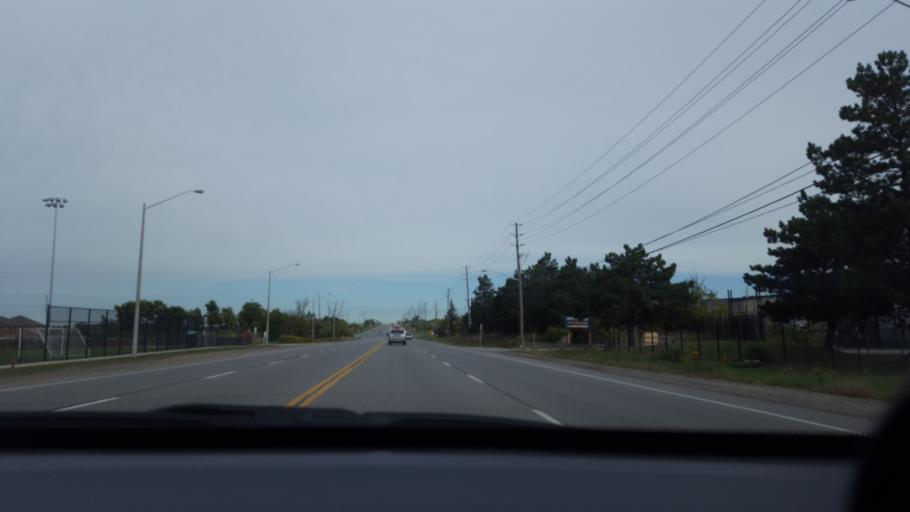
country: CA
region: Ontario
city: Vaughan
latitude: 43.8703
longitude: -79.5159
